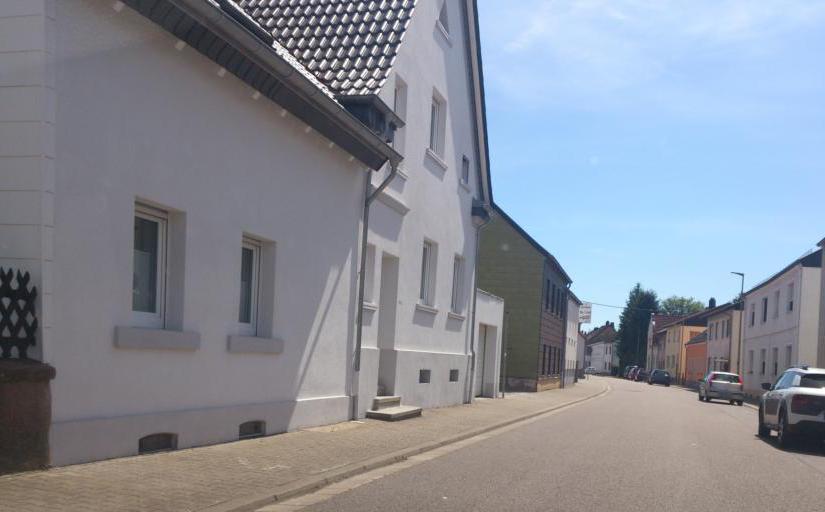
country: DE
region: Saarland
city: Bexbach
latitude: 49.3597
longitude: 7.2599
